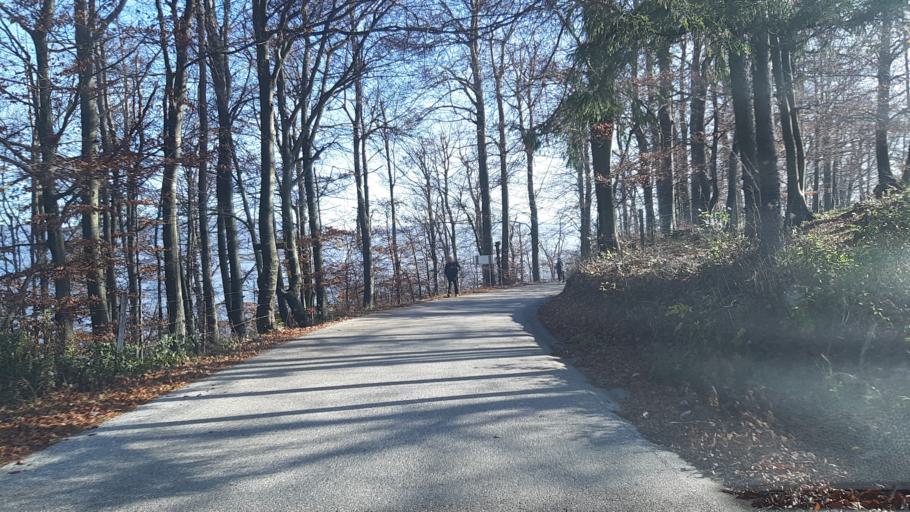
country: SI
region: Borovnica
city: Borovnica
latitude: 45.8936
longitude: 14.3580
